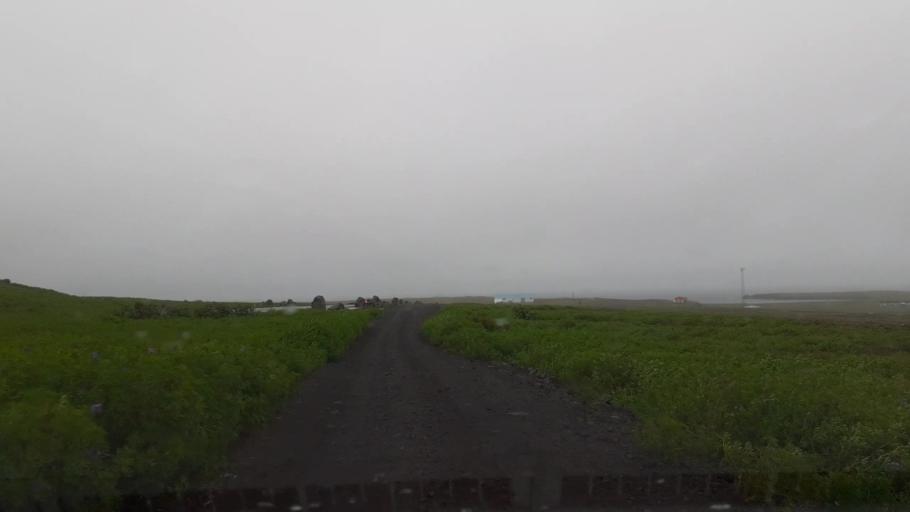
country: IS
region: Northeast
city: Husavik
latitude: 66.4600
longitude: -15.9634
